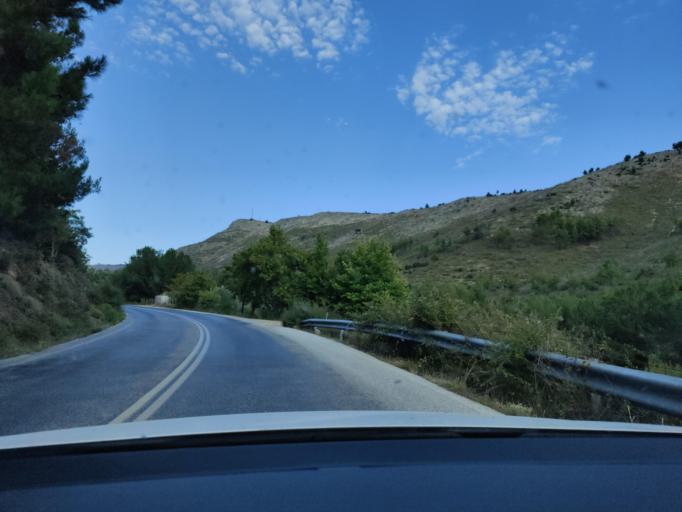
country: GR
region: East Macedonia and Thrace
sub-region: Nomos Kavalas
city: Limenaria
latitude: 40.6171
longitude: 24.6447
